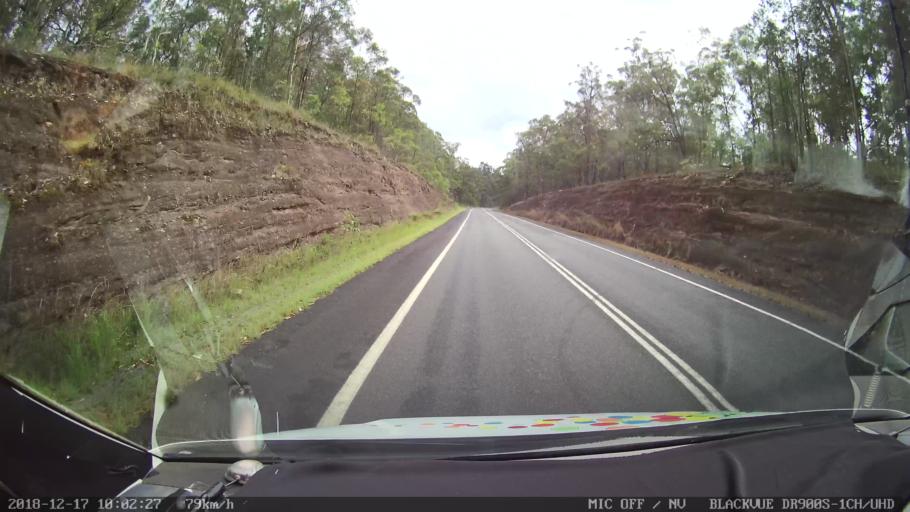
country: AU
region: New South Wales
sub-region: Tenterfield Municipality
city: Carrolls Creek
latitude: -28.9023
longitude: 152.4518
